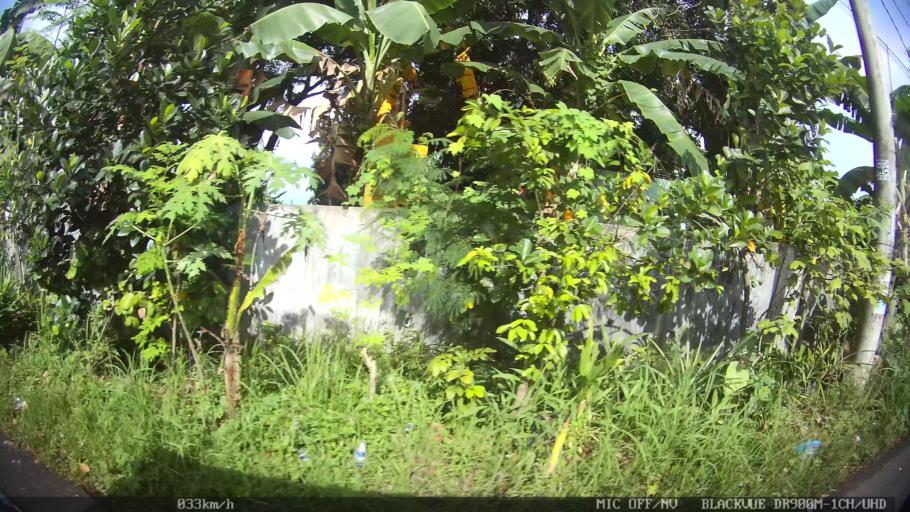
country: ID
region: North Sumatra
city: Medan
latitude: 3.6129
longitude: 98.6600
